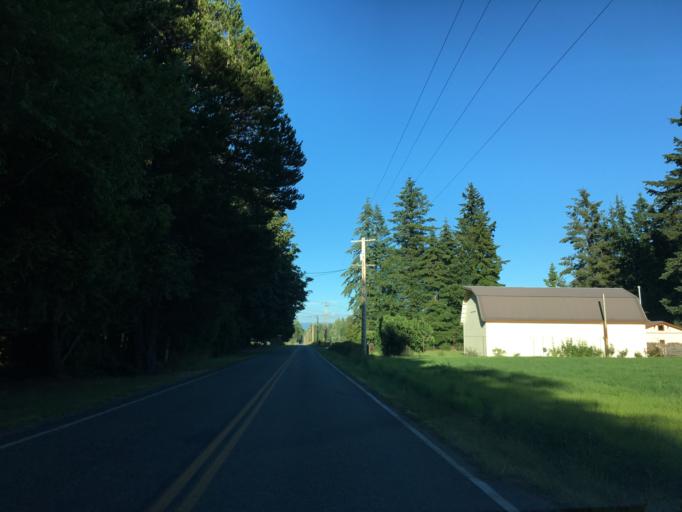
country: US
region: Washington
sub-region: Whatcom County
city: Ferndale
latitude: 48.9135
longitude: -122.6182
